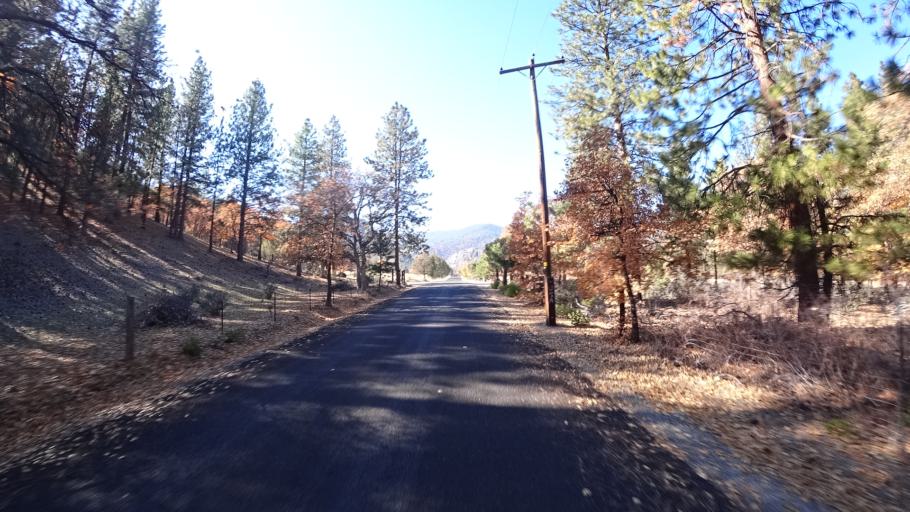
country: US
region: California
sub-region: Siskiyou County
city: Weed
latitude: 41.5035
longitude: -122.5822
